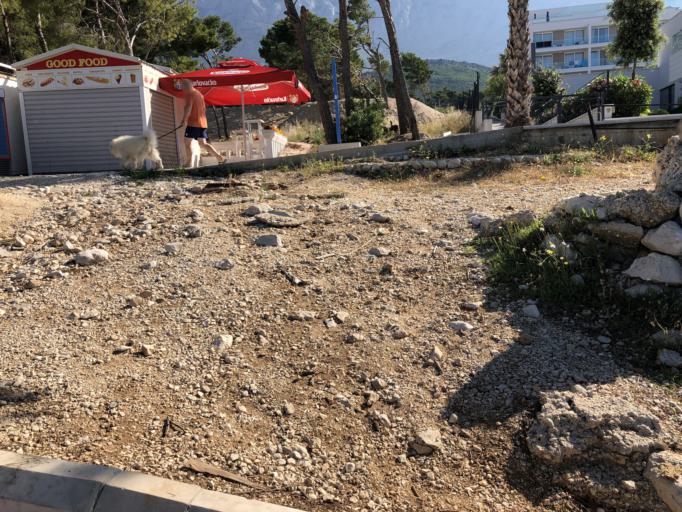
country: HR
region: Splitsko-Dalmatinska
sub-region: Grad Makarska
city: Makarska
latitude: 43.3068
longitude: 17.0008
